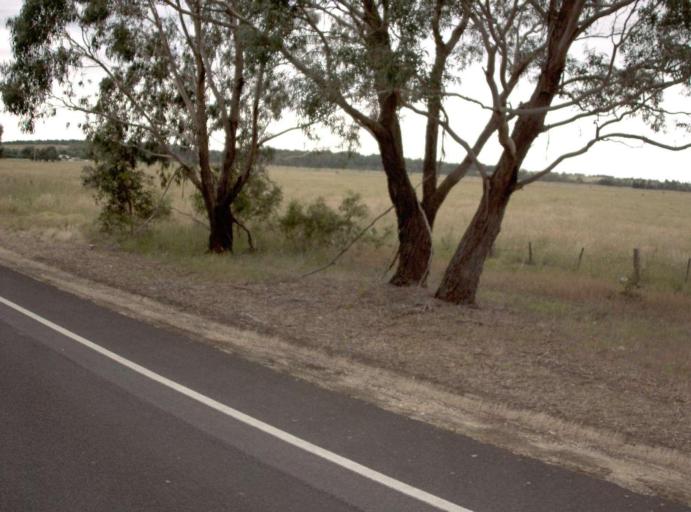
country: AU
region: Victoria
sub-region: Wellington
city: Sale
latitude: -38.3033
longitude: 147.0316
